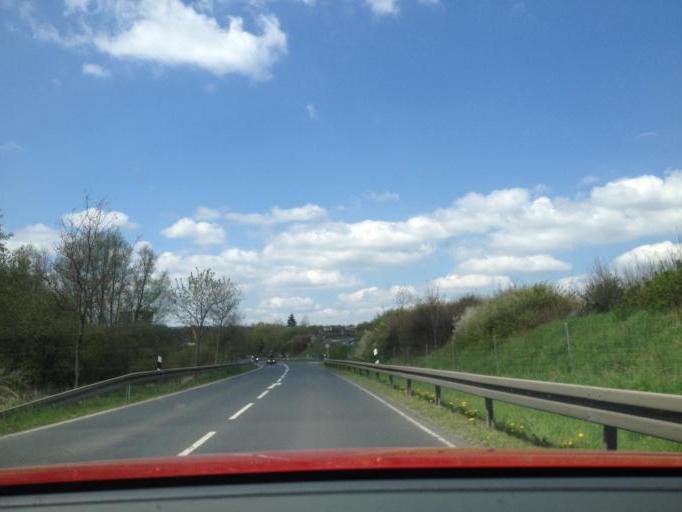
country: DE
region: Bavaria
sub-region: Upper Franconia
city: Marktredwitz
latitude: 50.0024
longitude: 12.1143
